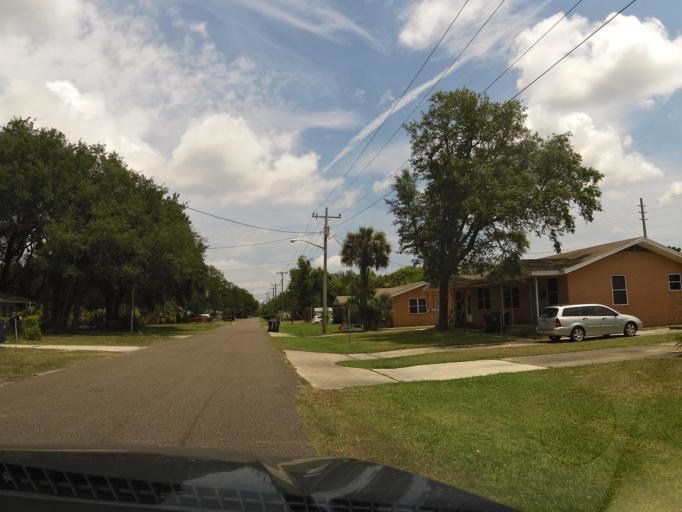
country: US
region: Florida
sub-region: Nassau County
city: Fernandina Beach
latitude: 30.6583
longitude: -81.4590
